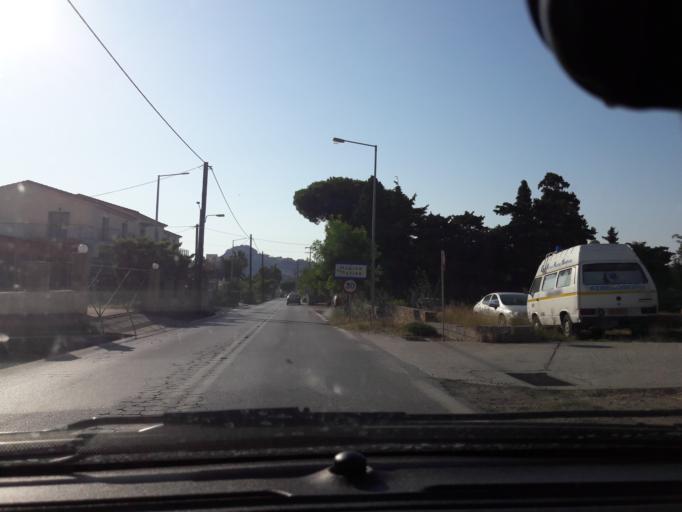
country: GR
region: North Aegean
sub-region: Nomos Lesvou
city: Myrina
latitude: 39.8705
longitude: 25.0696
